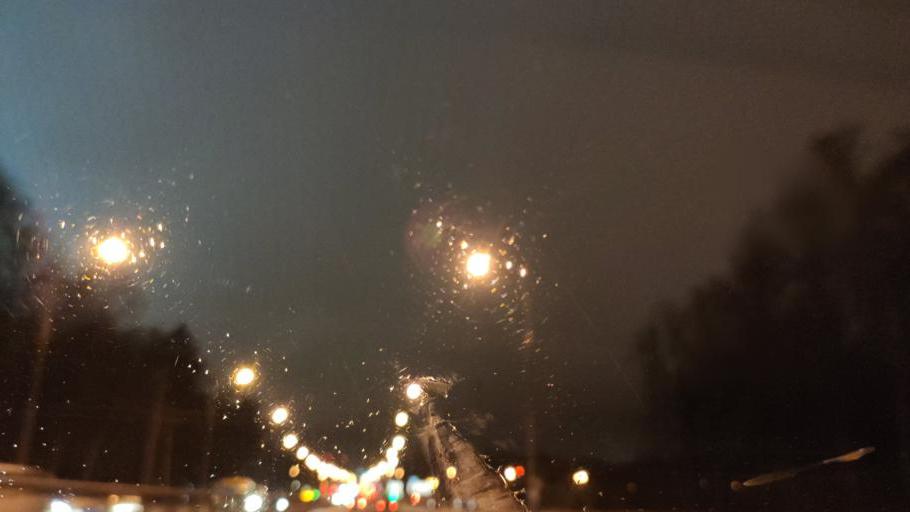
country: RU
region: Moskovskaya
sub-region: Leninskiy Rayon
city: Vnukovo
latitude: 55.6036
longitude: 37.3008
